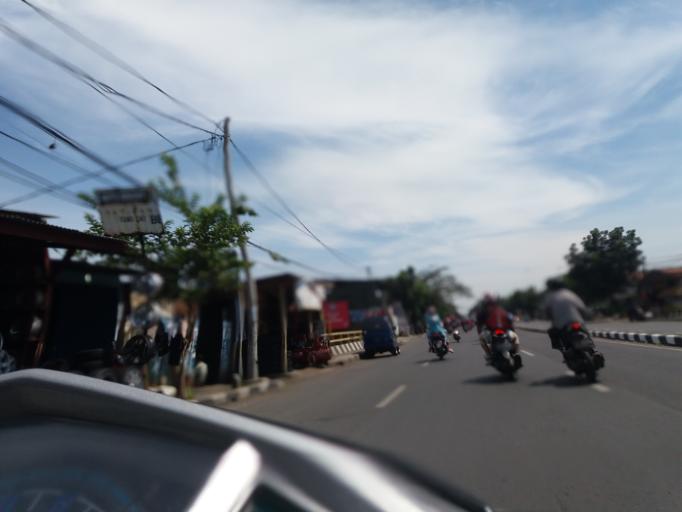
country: ID
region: West Java
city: Margahayukencana
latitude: -6.9481
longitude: 107.6044
